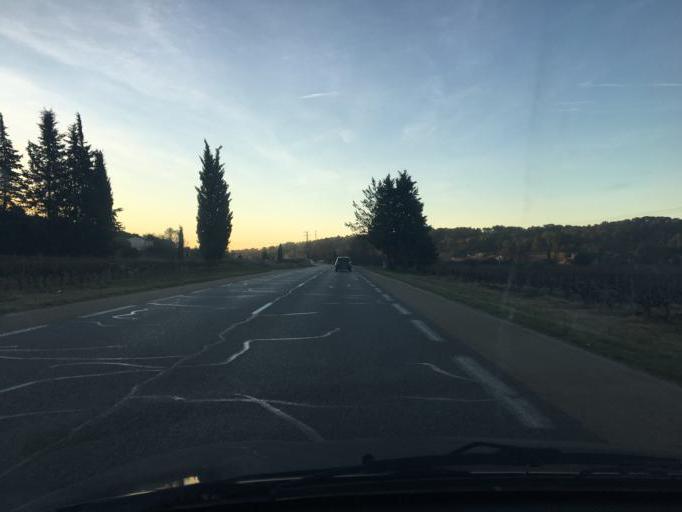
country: FR
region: Provence-Alpes-Cote d'Azur
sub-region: Departement du Var
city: Lorgues
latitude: 43.4809
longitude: 6.3710
